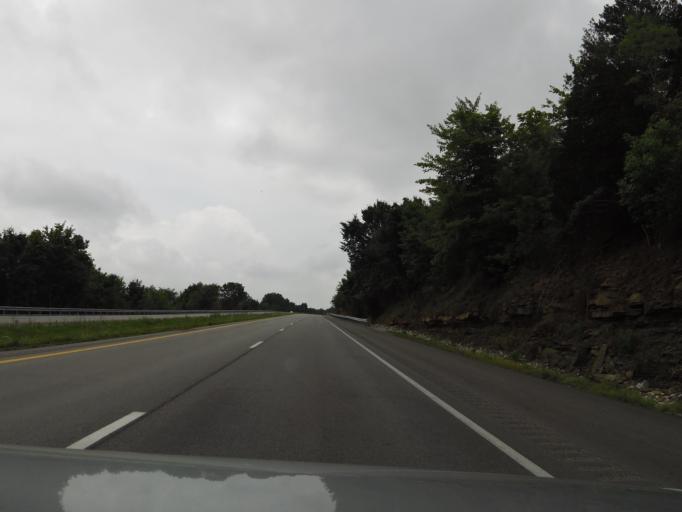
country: US
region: Kentucky
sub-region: Grayson County
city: Leitchfield
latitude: 37.4291
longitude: -86.3859
